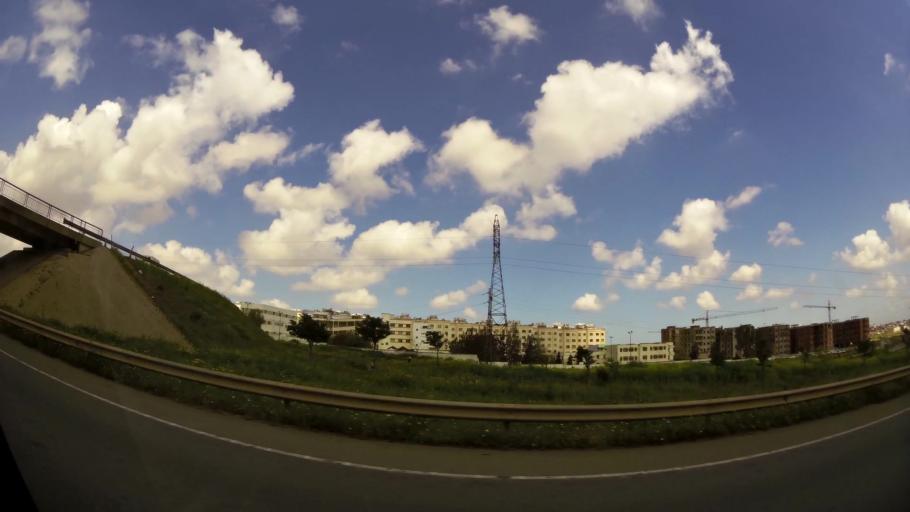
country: MA
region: Grand Casablanca
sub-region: Mediouna
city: Tit Mellil
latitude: 33.5352
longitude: -7.5488
